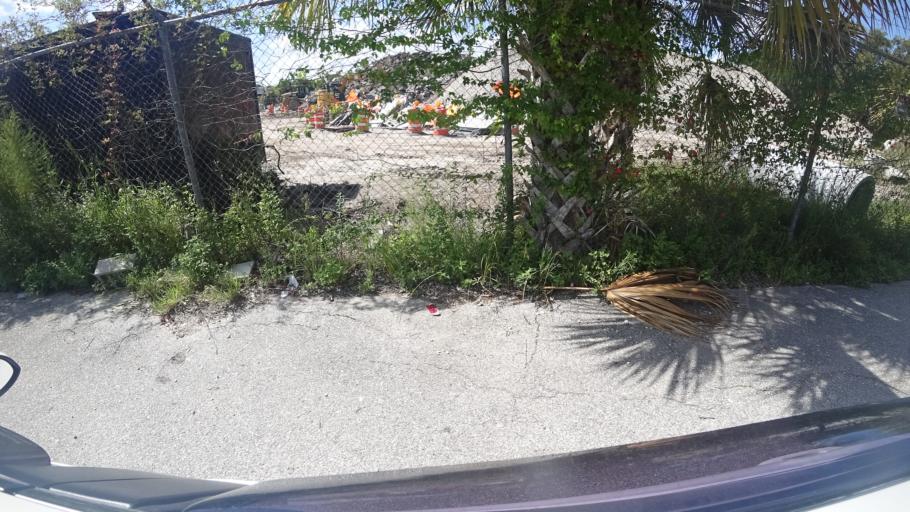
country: US
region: Florida
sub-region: Manatee County
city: Whitfield
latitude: 27.4226
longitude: -82.5435
